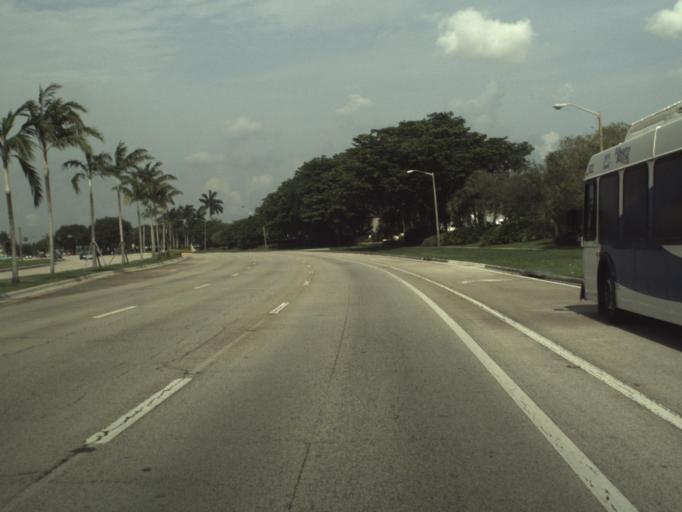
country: US
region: Florida
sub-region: Broward County
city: Tamarac
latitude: 26.1702
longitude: -80.2908
